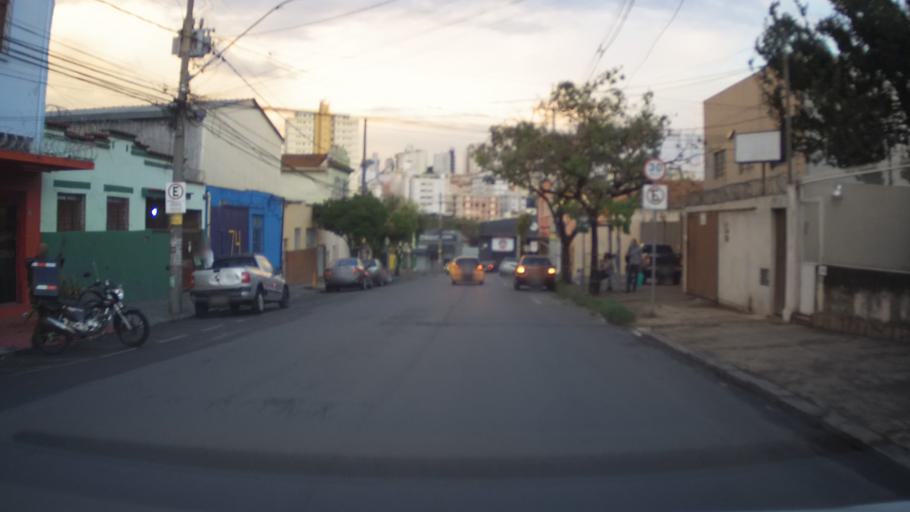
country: BR
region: Minas Gerais
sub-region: Belo Horizonte
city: Belo Horizonte
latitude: -19.9278
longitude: -43.9740
